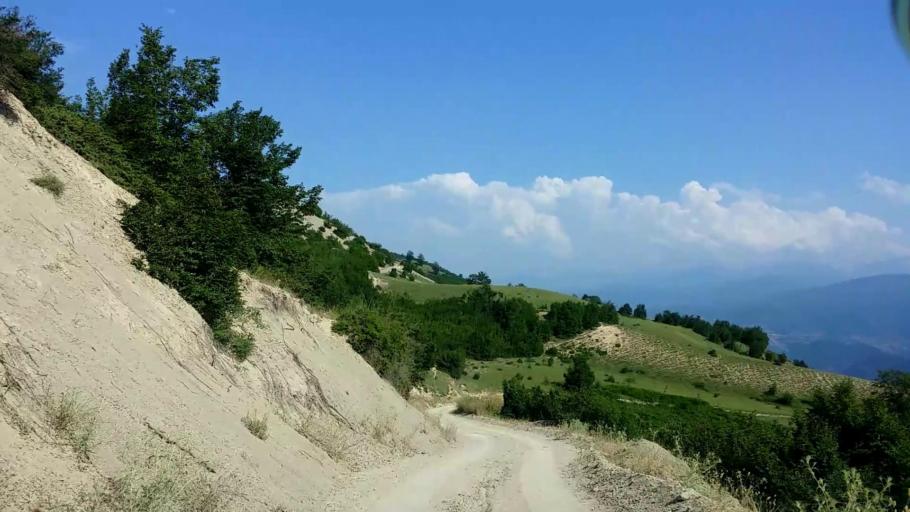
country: IR
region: Mazandaran
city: Chalus
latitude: 36.5513
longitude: 51.2948
